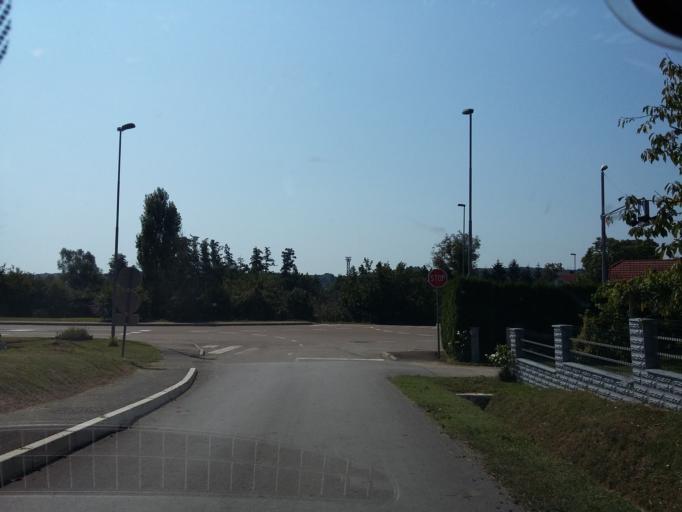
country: SI
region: Hodos-Hodos
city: Hodos
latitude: 46.8220
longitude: 16.3258
